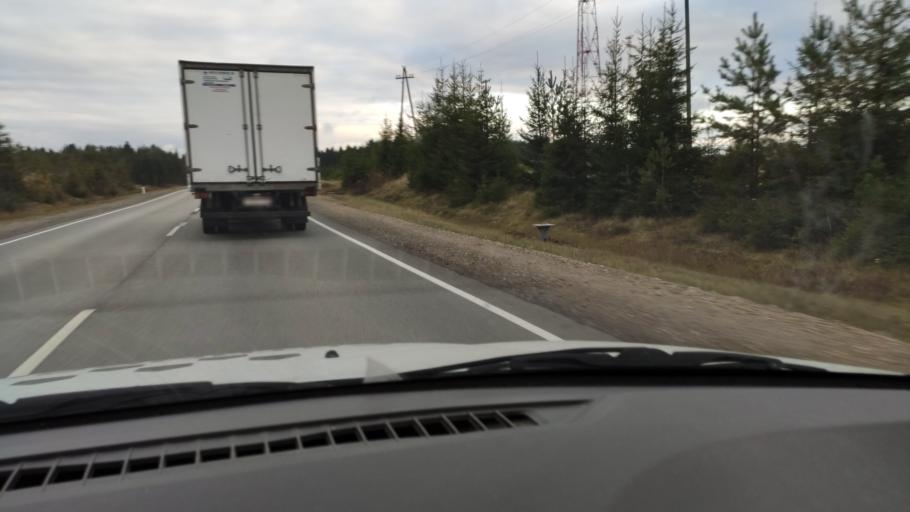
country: RU
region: Kirov
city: Chernaya Kholunitsa
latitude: 58.8552
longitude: 51.7271
